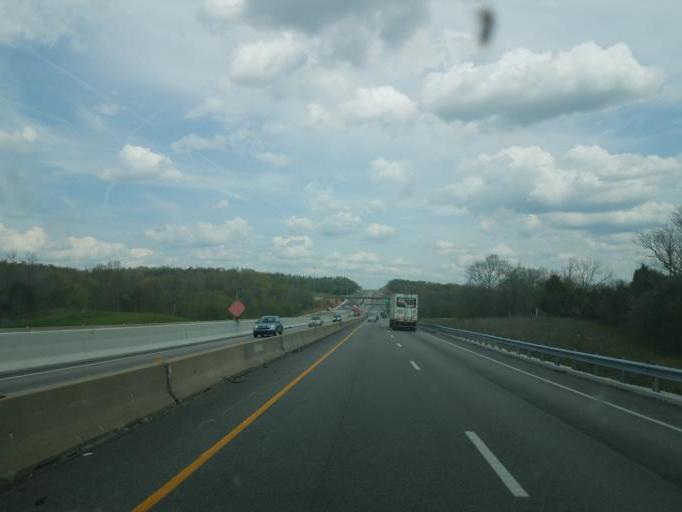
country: US
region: Kentucky
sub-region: Hart County
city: Munfordville
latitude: 37.3742
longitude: -85.8901
